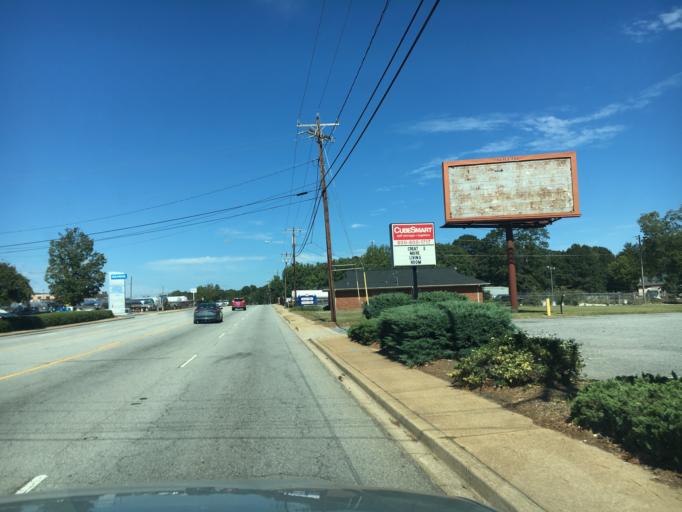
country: US
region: South Carolina
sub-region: Spartanburg County
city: Spartanburg
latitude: 34.9235
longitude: -81.8880
